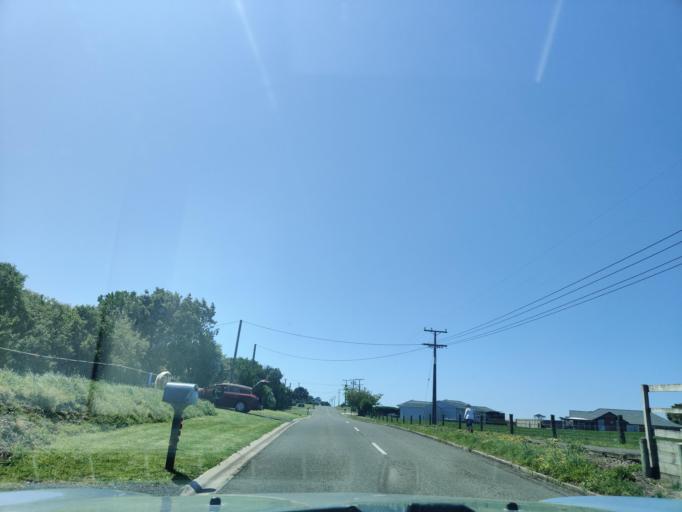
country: NZ
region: Taranaki
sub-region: South Taranaki District
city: Hawera
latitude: -39.6009
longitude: 174.2621
